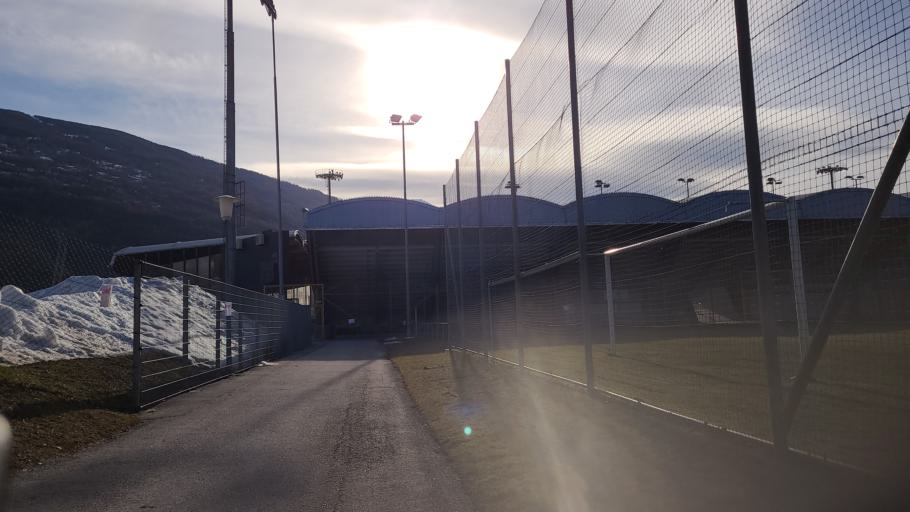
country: CH
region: Valais
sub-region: Sion District
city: Sitten
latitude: 46.2339
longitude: 7.3774
